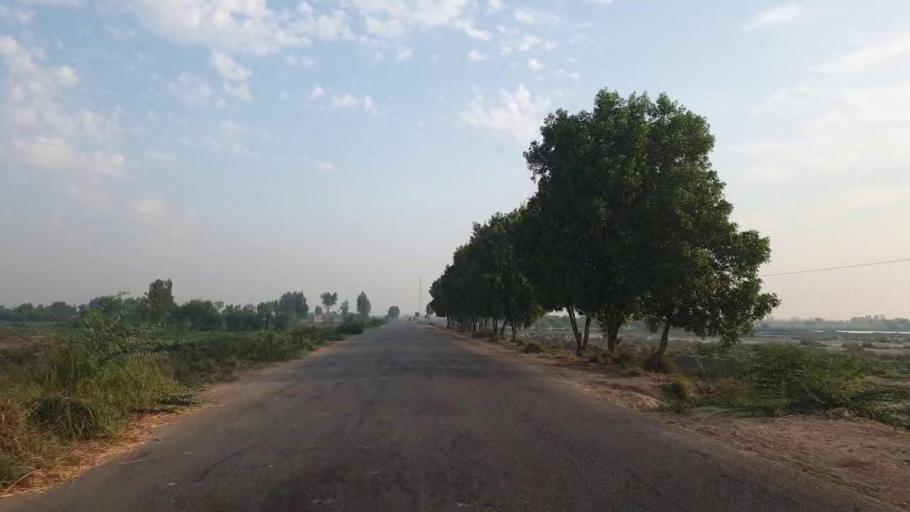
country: PK
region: Sindh
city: Badin
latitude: 24.6912
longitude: 68.9167
